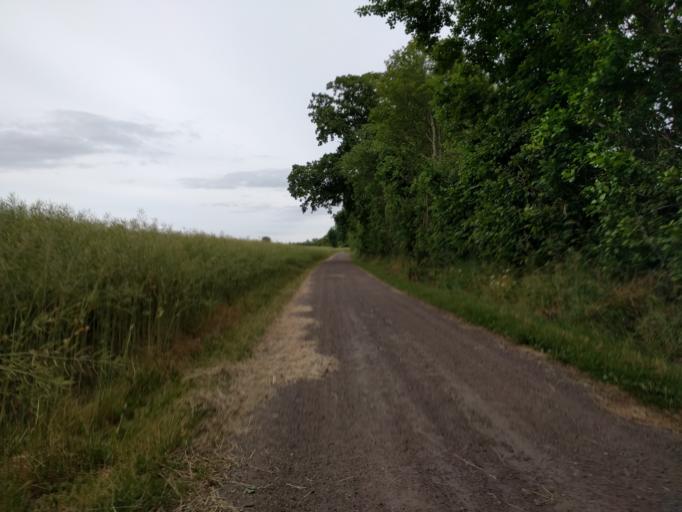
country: DK
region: South Denmark
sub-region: Kerteminde Kommune
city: Langeskov
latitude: 55.3971
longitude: 10.5814
